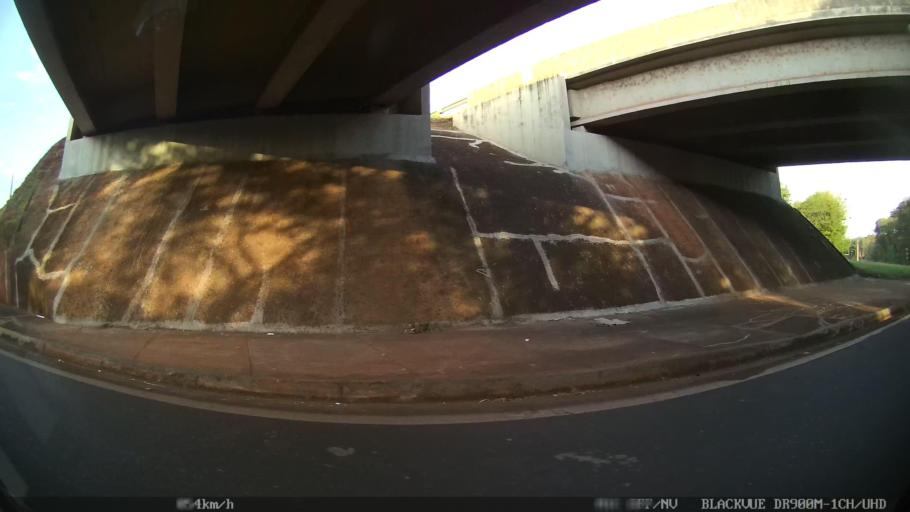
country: BR
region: Sao Paulo
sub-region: Ribeirao Preto
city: Ribeirao Preto
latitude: -21.1070
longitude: -47.8103
